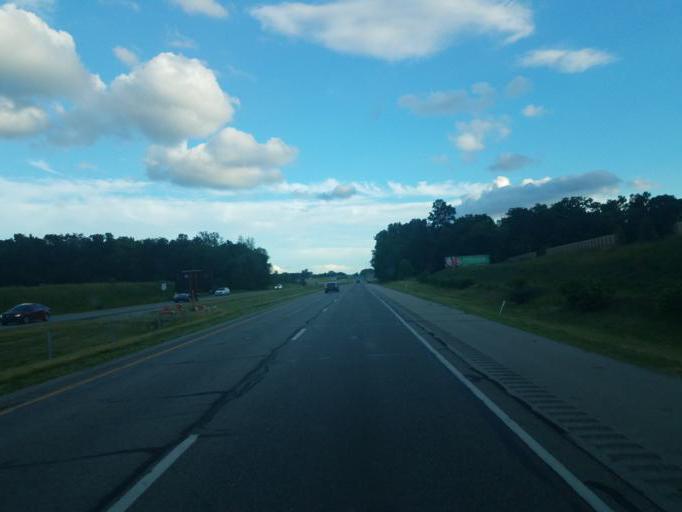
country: US
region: Indiana
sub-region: Allen County
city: Huntertown
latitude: 41.2091
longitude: -85.1047
